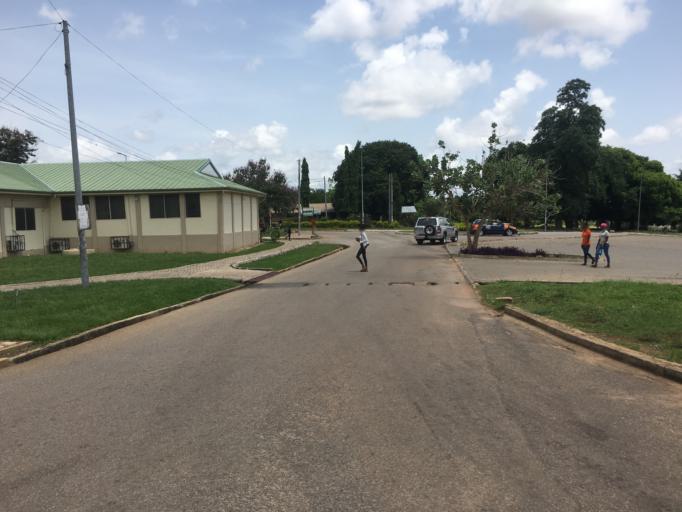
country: GH
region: Ashanti
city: Kumasi
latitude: 6.6830
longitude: -1.5766
